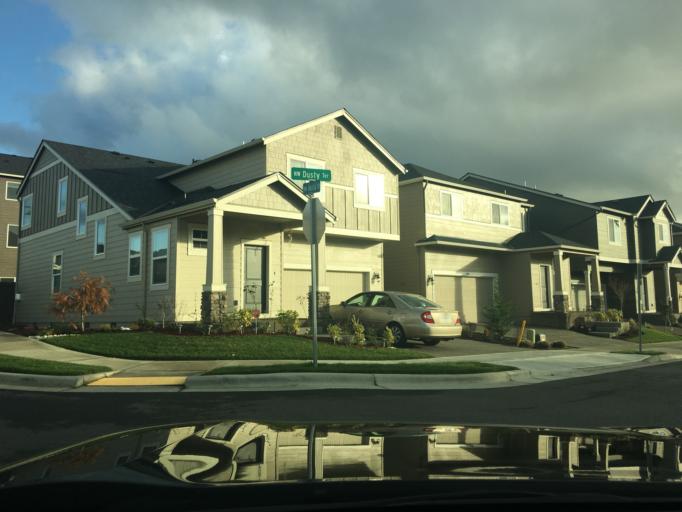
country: US
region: Oregon
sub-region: Washington County
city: Bethany
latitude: 45.5728
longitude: -122.8510
